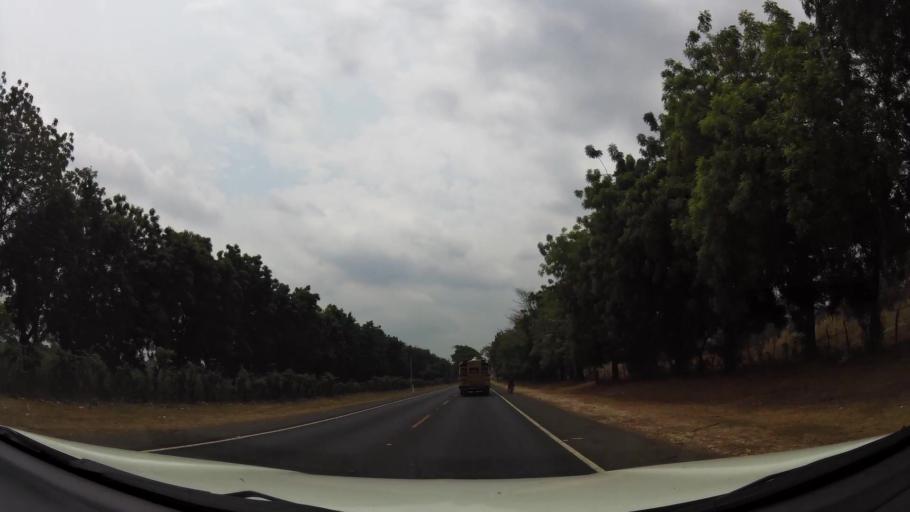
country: NI
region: Leon
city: Telica
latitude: 12.5037
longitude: -86.8602
